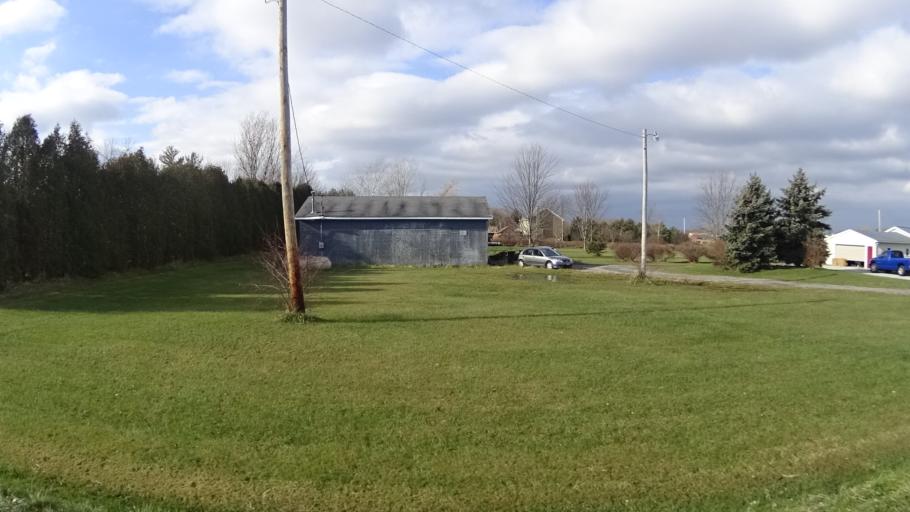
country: US
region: Ohio
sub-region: Lorain County
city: Camden
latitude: 41.2863
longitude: -82.2884
